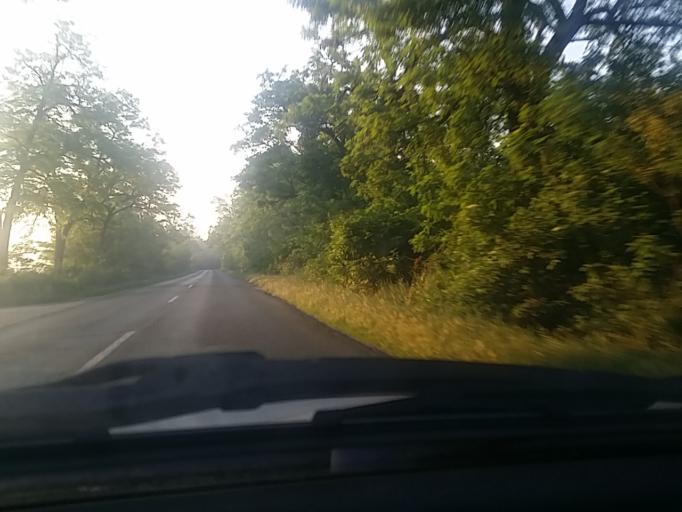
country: HU
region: Pest
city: Forropuszta
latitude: 47.4570
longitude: 19.6668
